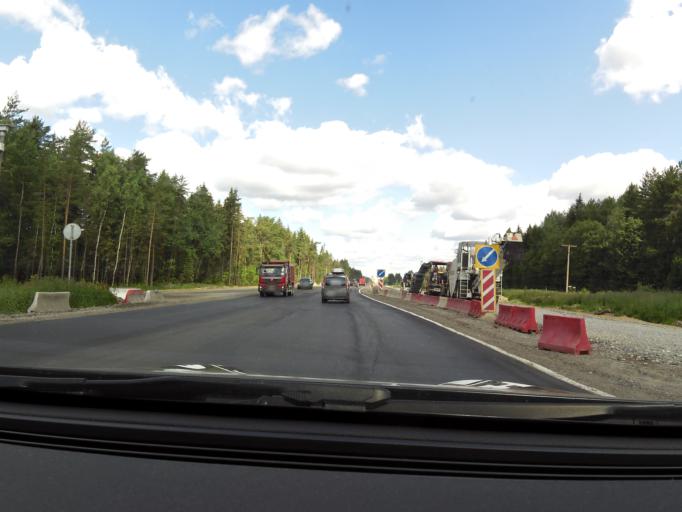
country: RU
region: Tverskaya
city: Torzhok
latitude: 57.0900
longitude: 34.9988
